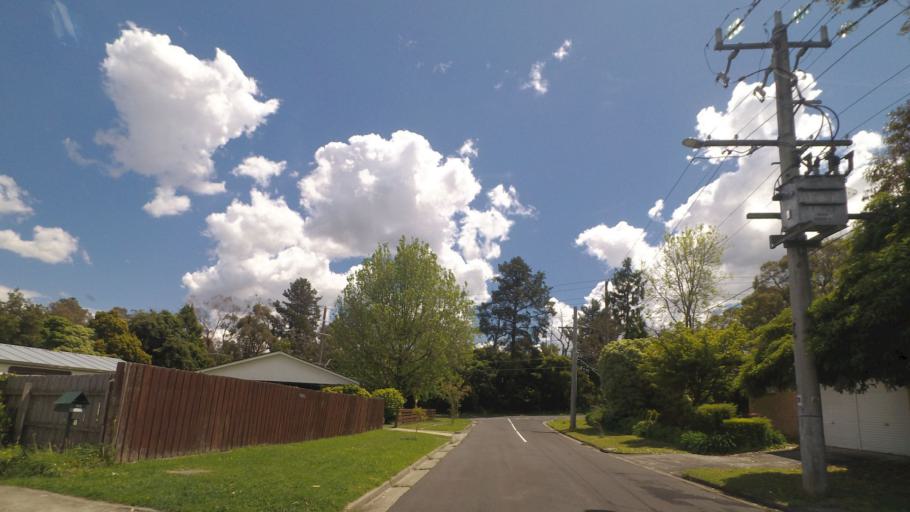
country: AU
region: Victoria
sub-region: Maroondah
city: Ringwood East
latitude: -37.8111
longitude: 145.2555
